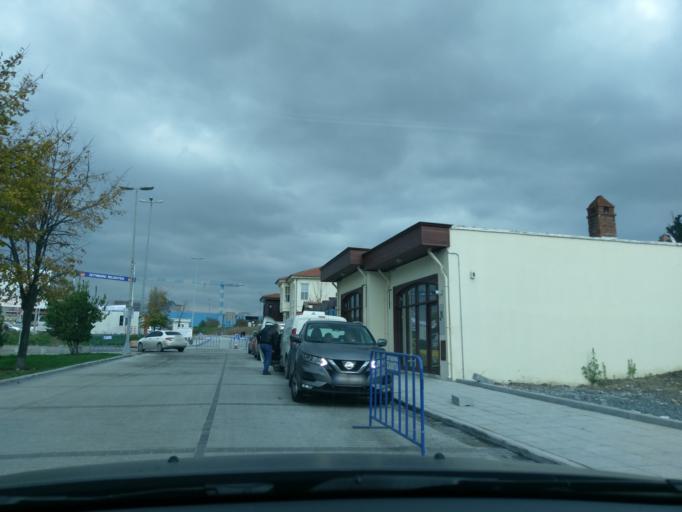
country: TR
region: Istanbul
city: Zeytinburnu
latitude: 41.0145
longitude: 28.9189
